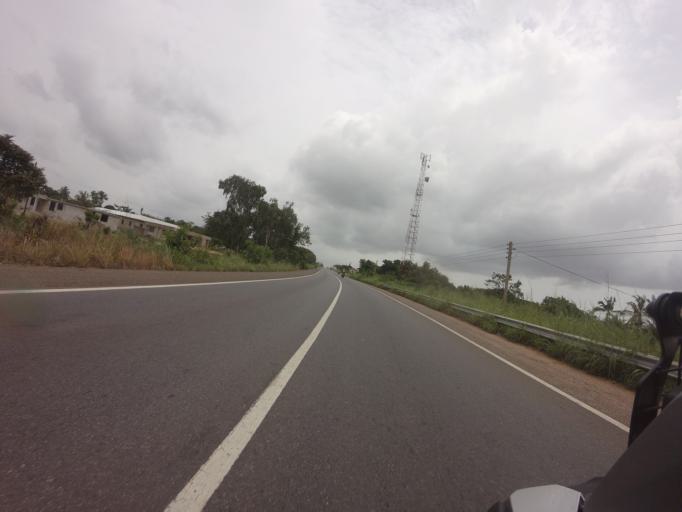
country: GH
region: Volta
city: Keta
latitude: 6.0623
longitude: 0.8675
